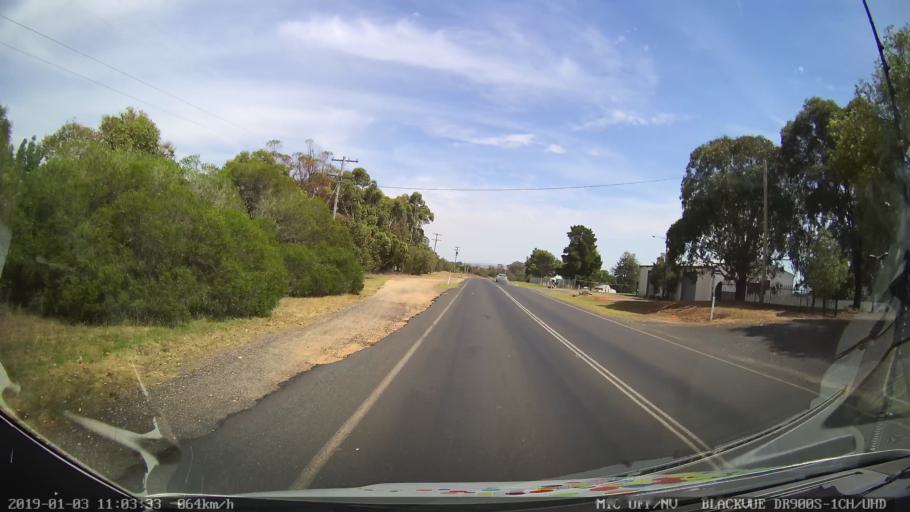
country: AU
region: New South Wales
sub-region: Young
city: Young
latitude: -34.2894
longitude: 148.2939
